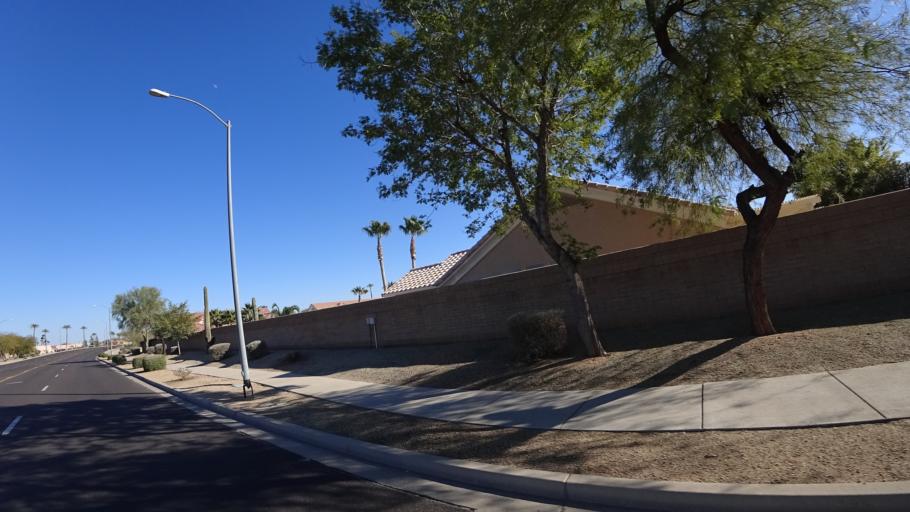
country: US
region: Arizona
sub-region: Maricopa County
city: Sun City West
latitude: 33.6873
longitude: -112.3640
